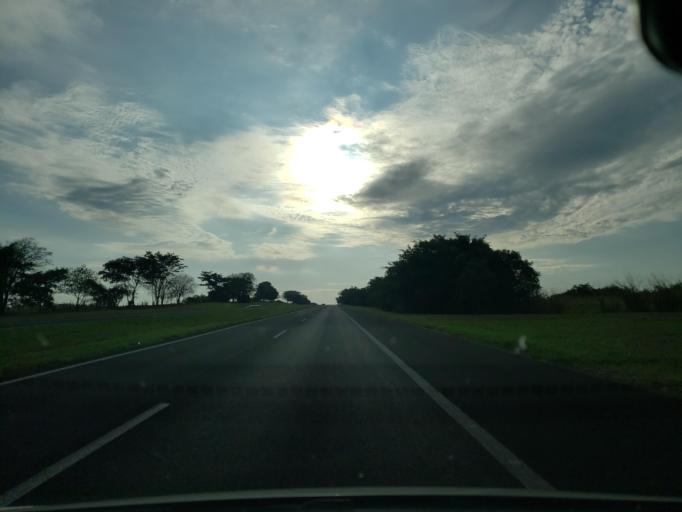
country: BR
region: Sao Paulo
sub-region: Mirandopolis
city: Mirandopolis
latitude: -21.1163
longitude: -51.0151
